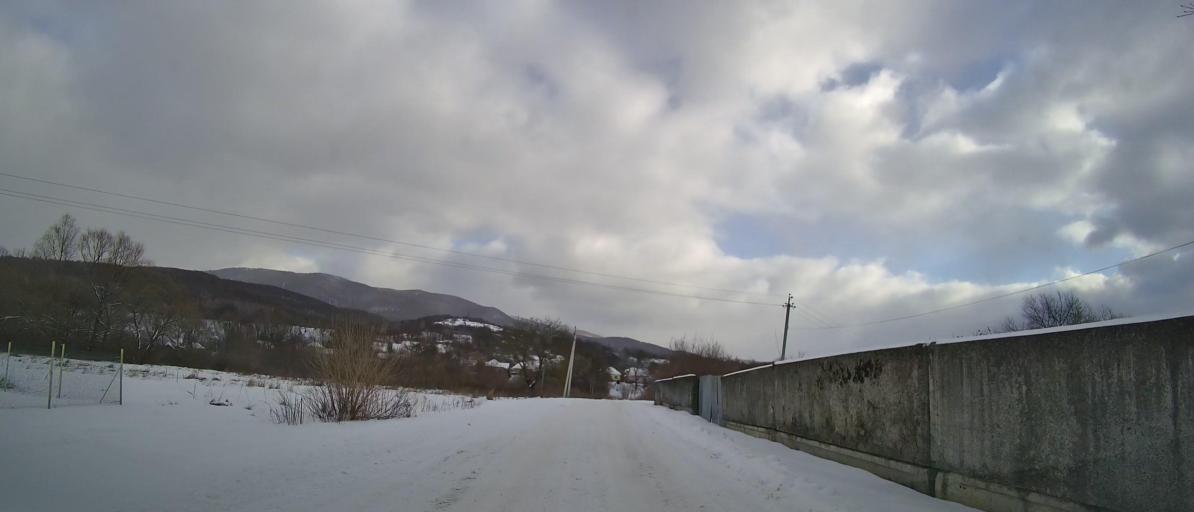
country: UA
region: Zakarpattia
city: Velykyi Bereznyi
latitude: 48.9236
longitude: 22.4612
